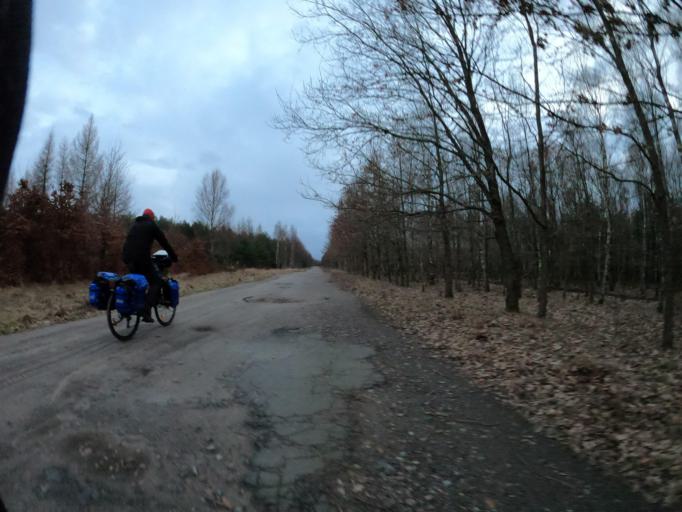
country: PL
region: West Pomeranian Voivodeship
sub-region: Powiat szczecinecki
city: Borne Sulinowo
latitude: 53.5355
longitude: 16.5778
